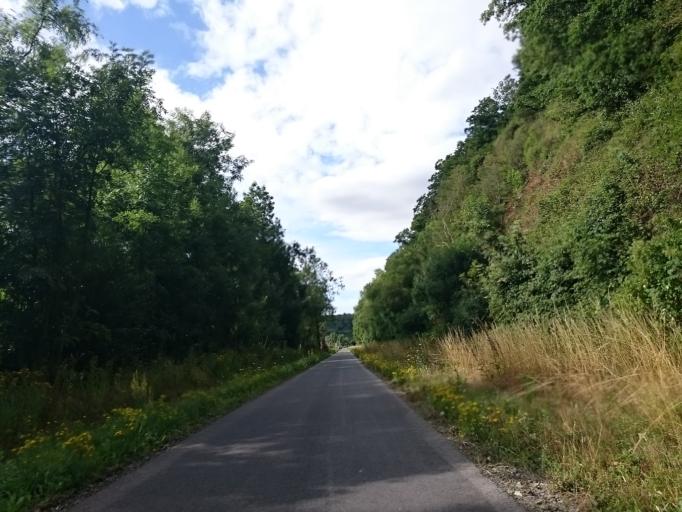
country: FR
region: Lower Normandy
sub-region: Departement du Calvados
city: Thury-Harcourt
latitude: 49.0300
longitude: -0.4649
